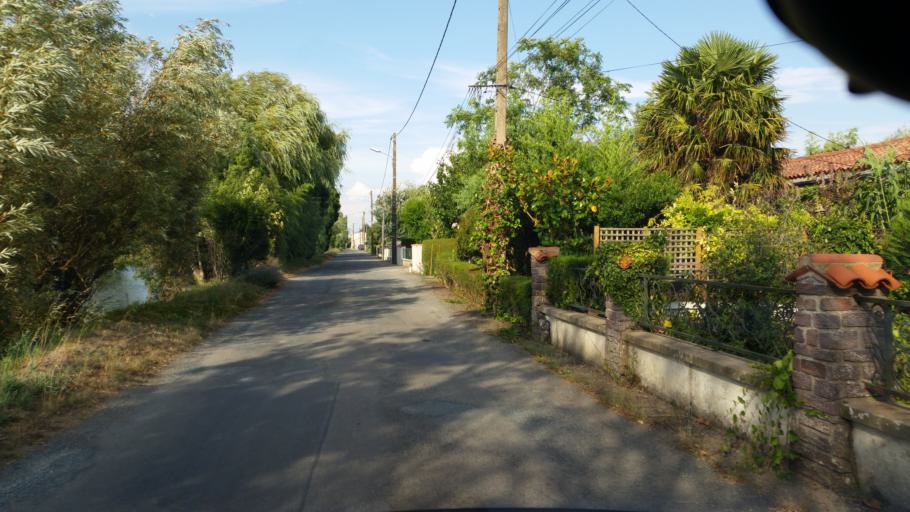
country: FR
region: Poitou-Charentes
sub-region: Departement de la Charente-Maritime
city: Marans
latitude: 46.3157
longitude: -0.9794
